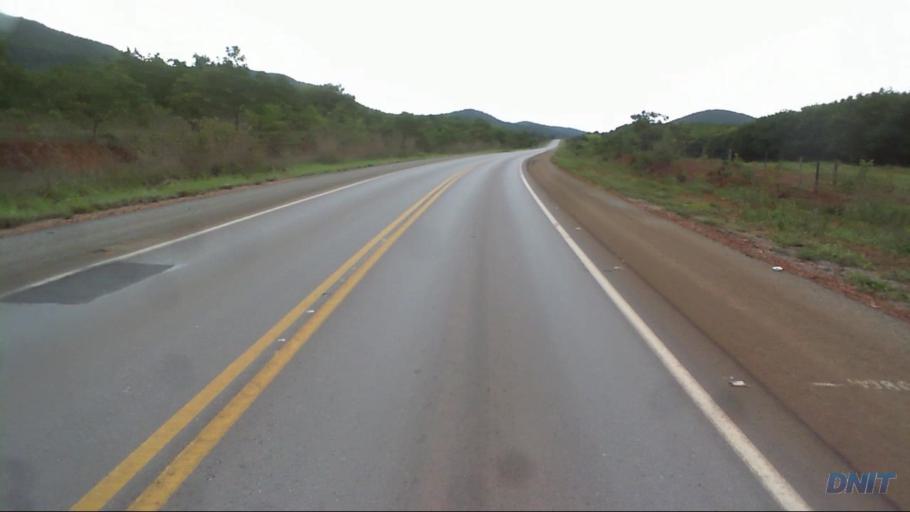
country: BR
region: Goias
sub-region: Barro Alto
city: Barro Alto
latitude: -14.8978
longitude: -48.9667
